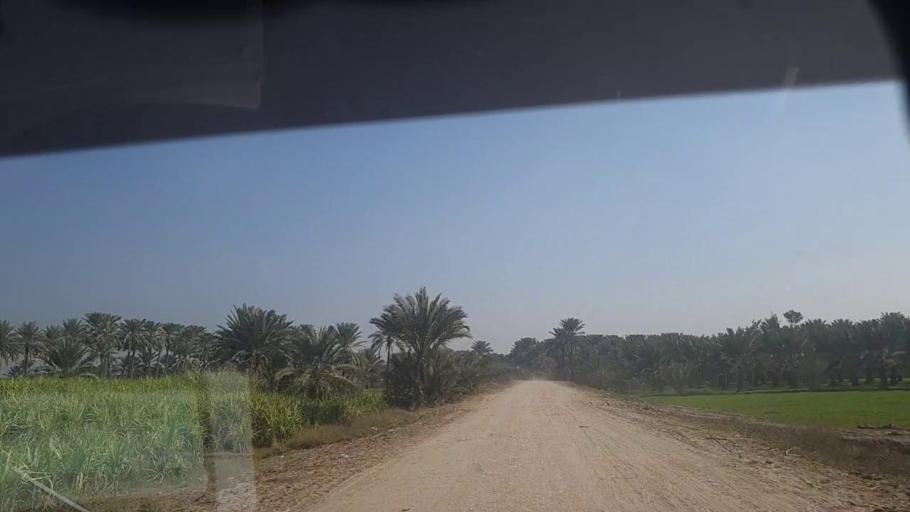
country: PK
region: Sindh
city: Khairpur
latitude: 27.4573
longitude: 68.7502
